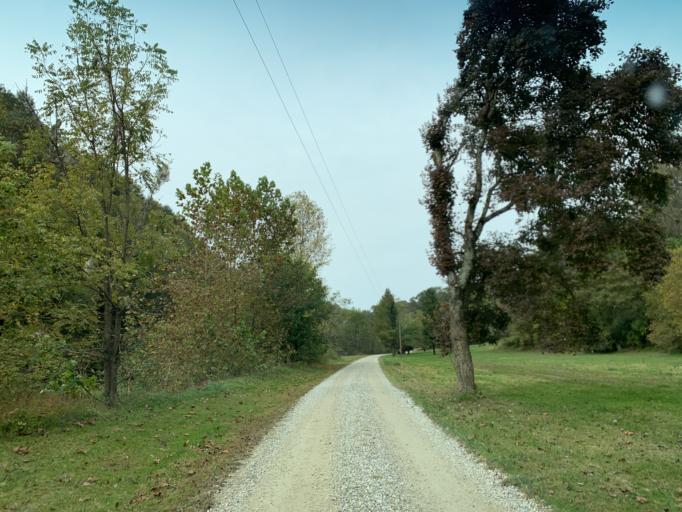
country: US
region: Pennsylvania
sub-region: York County
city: Susquehanna Trails
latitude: 39.7932
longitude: -76.4235
